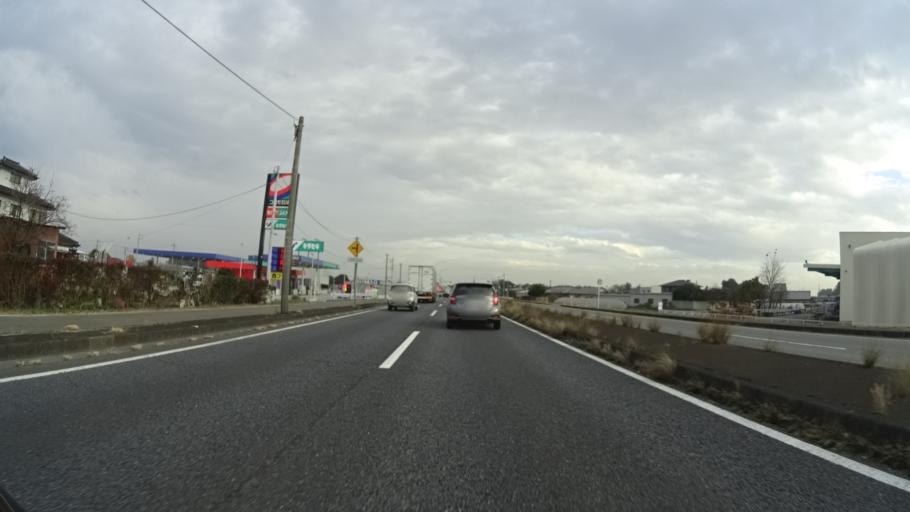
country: JP
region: Gunma
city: Isesaki
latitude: 36.3584
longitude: 139.2015
